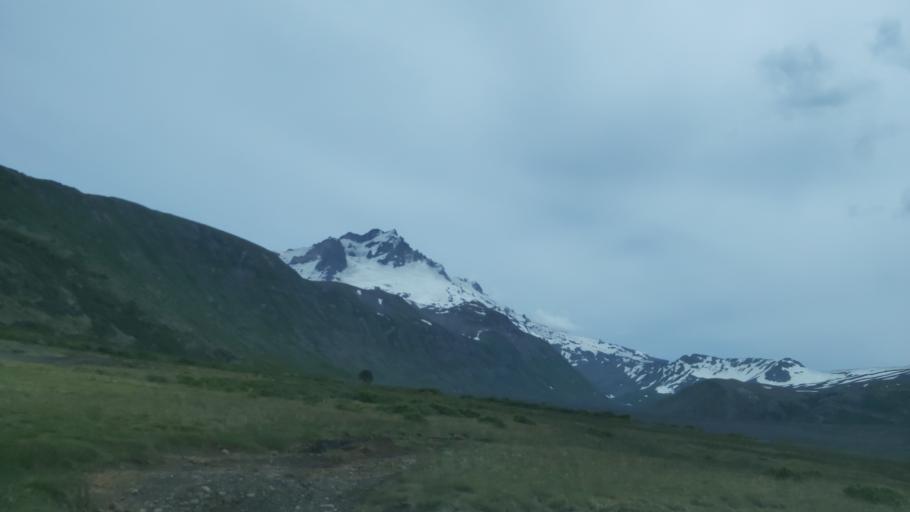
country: AR
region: Neuquen
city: Andacollo
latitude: -37.4618
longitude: -71.3157
